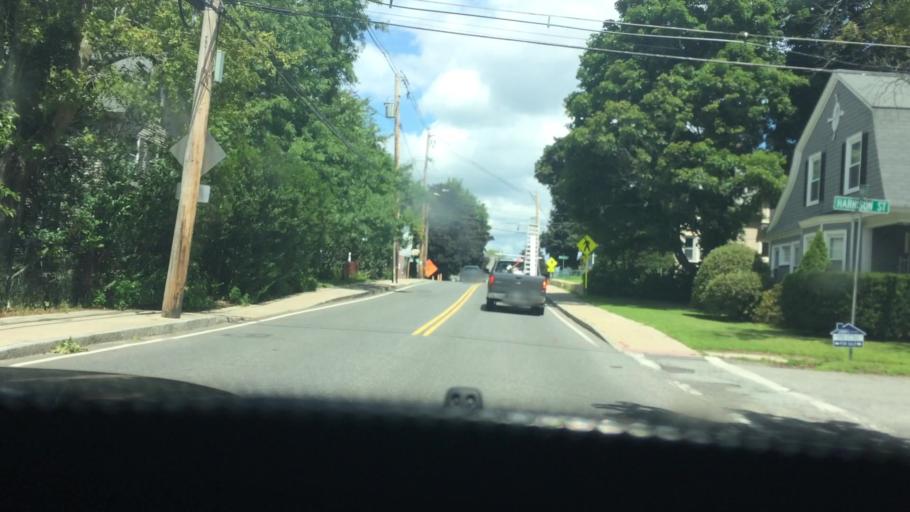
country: US
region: Massachusetts
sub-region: Middlesex County
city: Maynard
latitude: 42.4284
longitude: -71.4498
